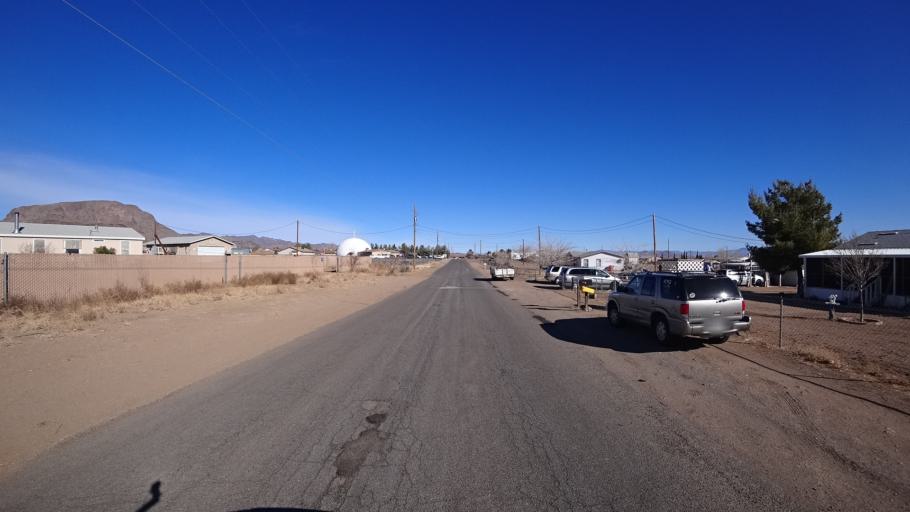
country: US
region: Arizona
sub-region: Mohave County
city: New Kingman-Butler
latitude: 35.2500
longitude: -114.0350
